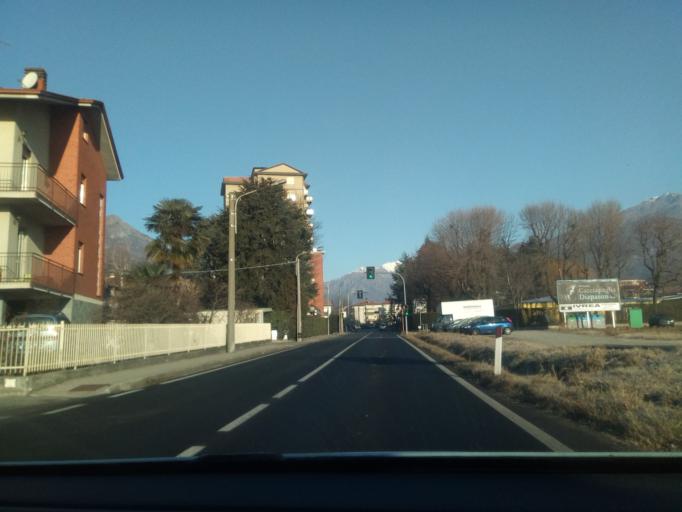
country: IT
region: Piedmont
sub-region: Provincia di Torino
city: Montalto Dora
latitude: 45.4814
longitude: 7.8640
